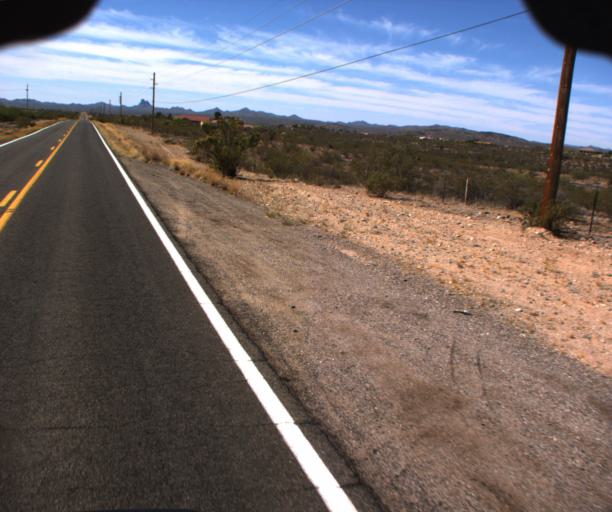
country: US
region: Arizona
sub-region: Yavapai County
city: Congress
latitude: 34.0505
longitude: -112.8160
